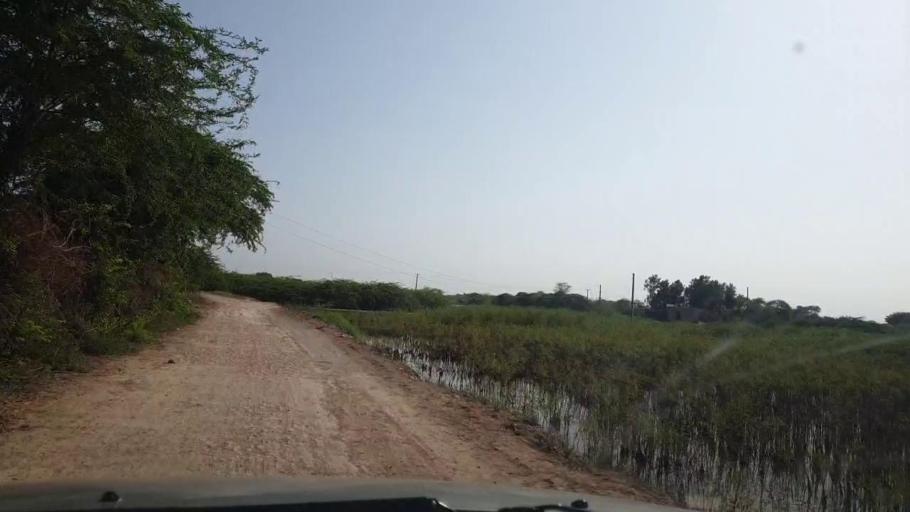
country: PK
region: Sindh
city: Mirwah Gorchani
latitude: 25.2525
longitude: 68.9393
